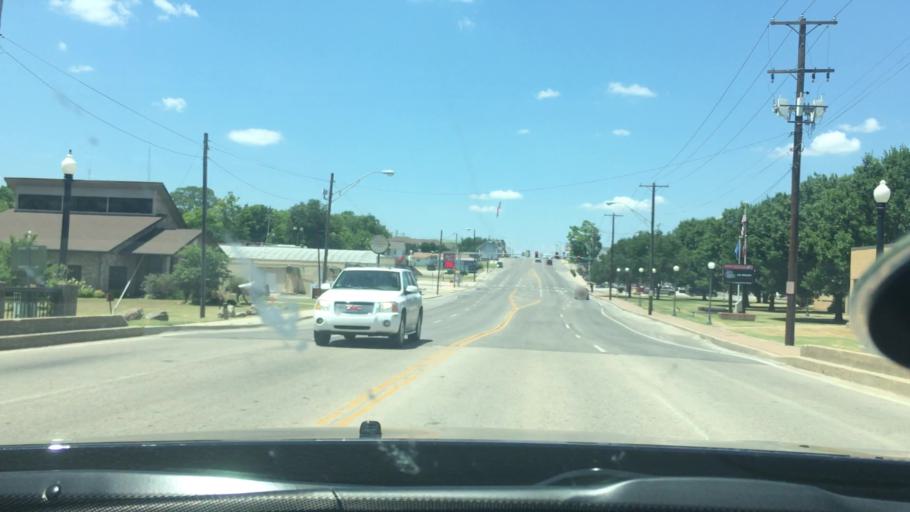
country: US
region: Oklahoma
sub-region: Murray County
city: Sulphur
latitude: 34.5065
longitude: -96.9763
